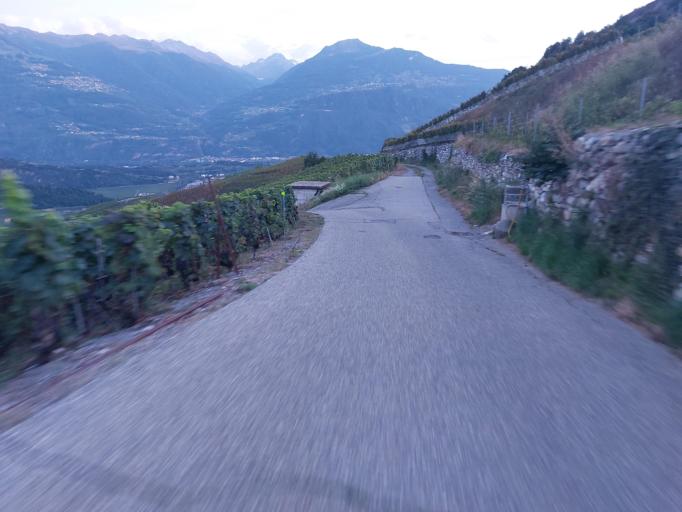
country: CH
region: Valais
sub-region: Conthey District
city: Conthey
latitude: 46.2494
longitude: 7.3051
